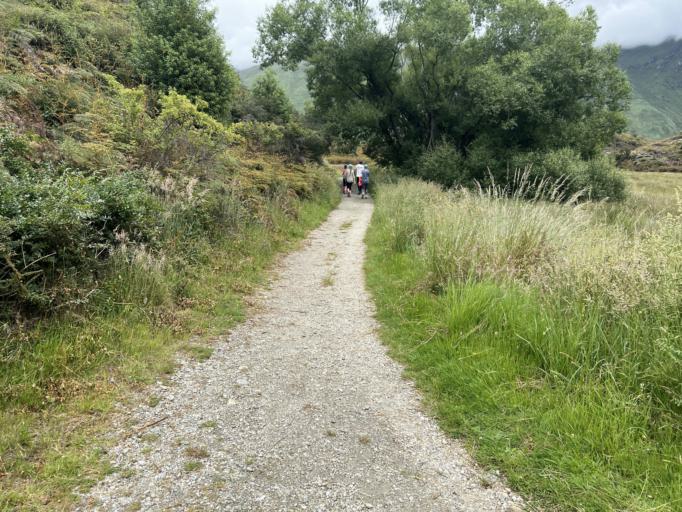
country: NZ
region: Otago
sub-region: Queenstown-Lakes District
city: Wanaka
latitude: -44.6494
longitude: 168.9626
